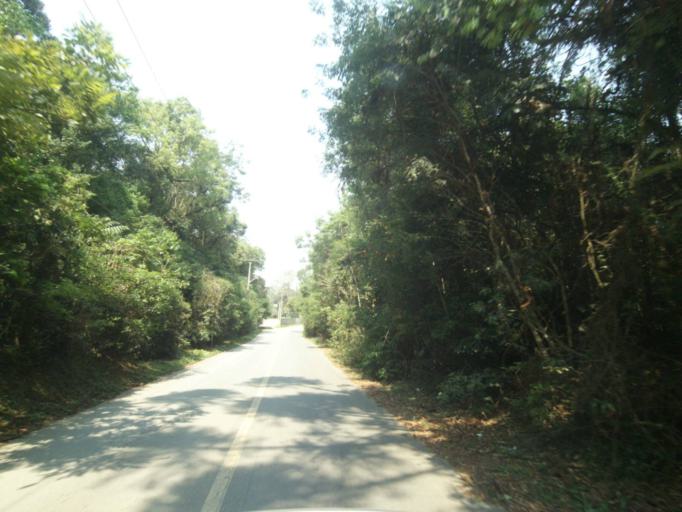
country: BR
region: Parana
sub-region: Sao Jose Dos Pinhais
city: Sao Jose dos Pinhais
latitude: -25.5554
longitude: -49.2317
